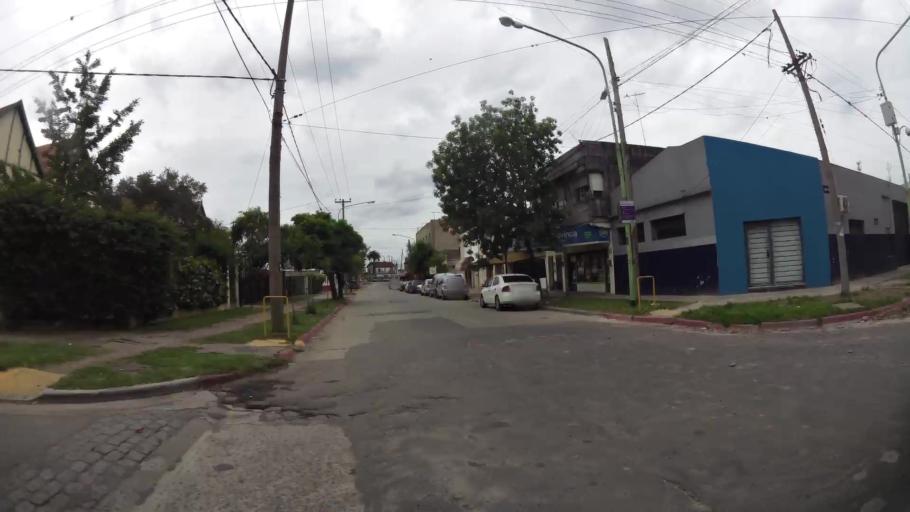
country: AR
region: Buenos Aires
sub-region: Partido de Campana
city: Campana
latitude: -34.1582
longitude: -58.9645
